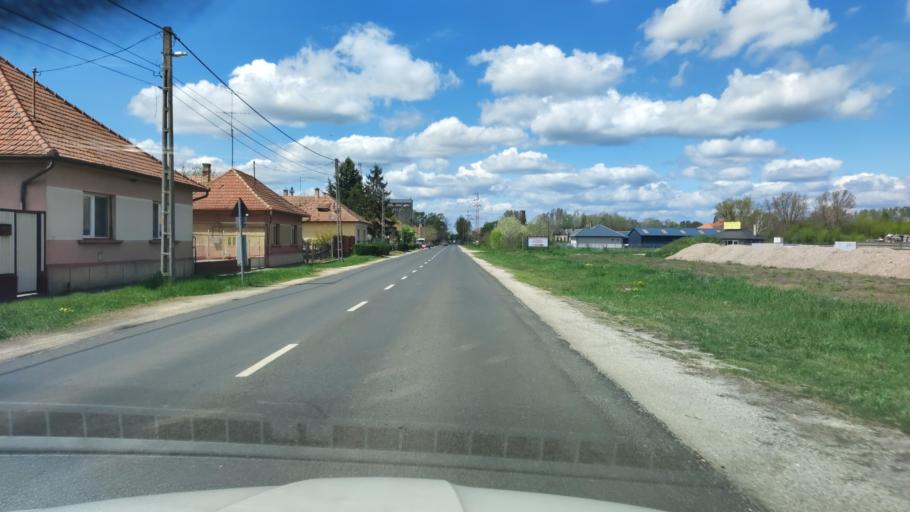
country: HU
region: Pest
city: Cegled
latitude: 47.1695
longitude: 19.8253
